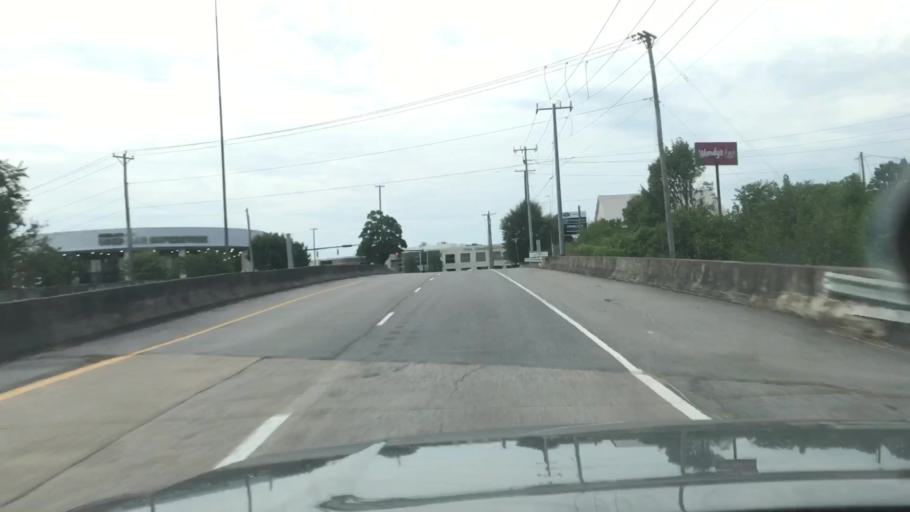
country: US
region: Tennessee
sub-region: Rutherford County
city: La Vergne
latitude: 36.0433
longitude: -86.6500
